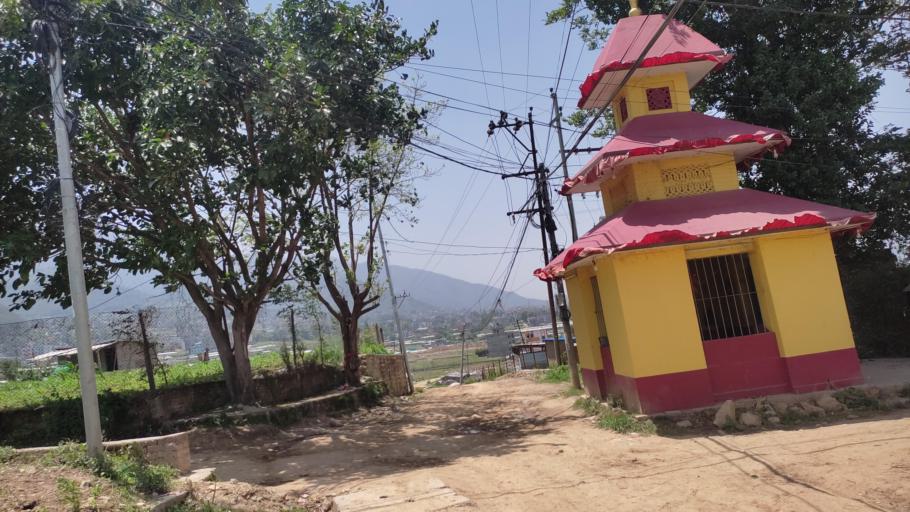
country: NP
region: Central Region
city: Kirtipur
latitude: 27.6703
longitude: 85.2617
